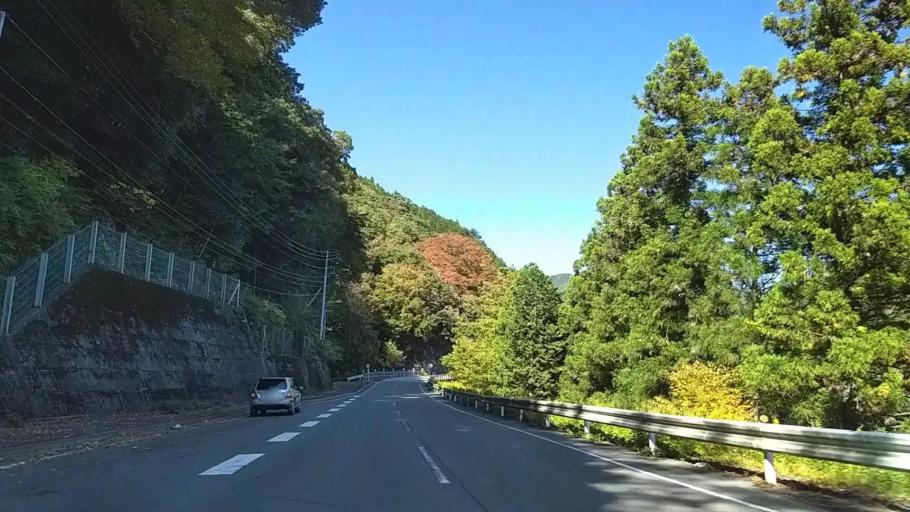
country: JP
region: Yamanashi
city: Uenohara
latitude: 35.6563
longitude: 139.0930
